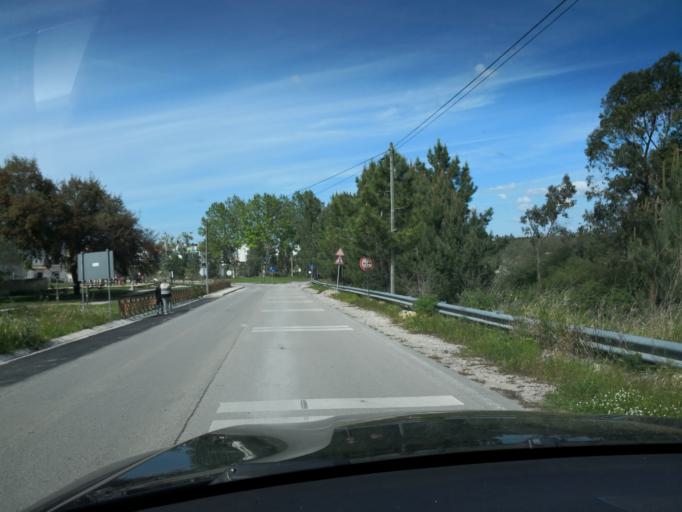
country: PT
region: Setubal
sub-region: Barreiro
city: Santo Antonio da Charneca
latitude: 38.5519
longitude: -9.0407
